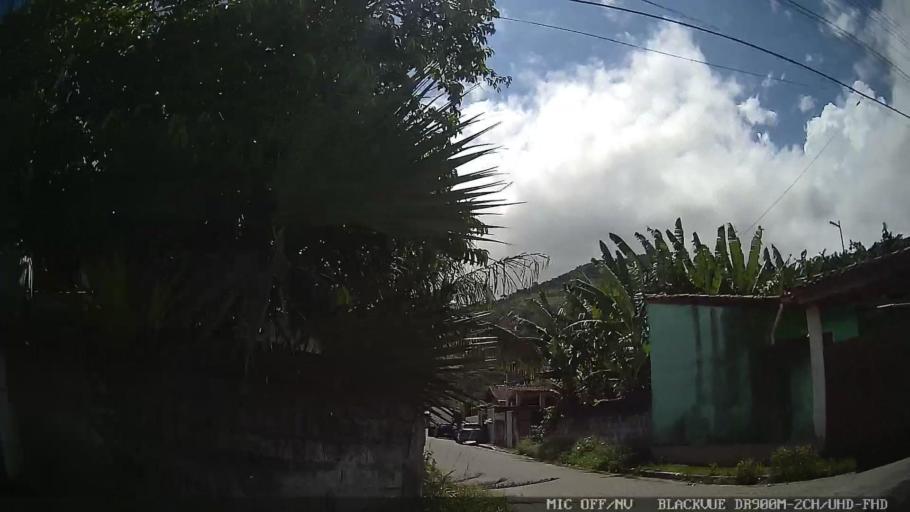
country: BR
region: Sao Paulo
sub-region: Caraguatatuba
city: Caraguatatuba
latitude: -23.6279
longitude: -45.4383
